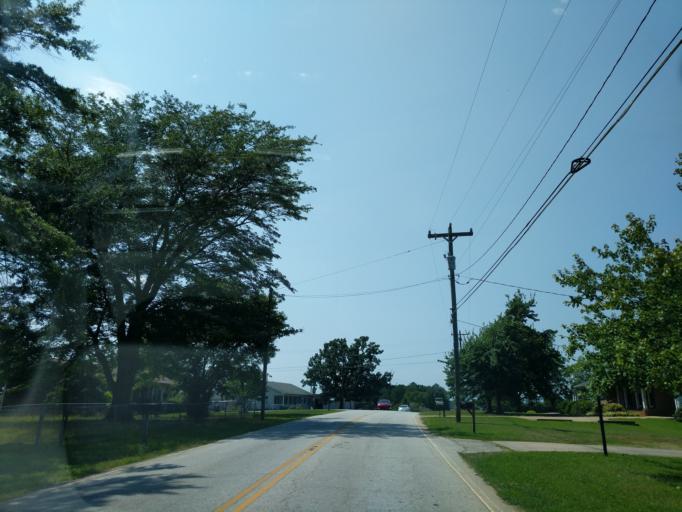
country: US
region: South Carolina
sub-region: Spartanburg County
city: Duncan
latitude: 34.9523
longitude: -82.1655
